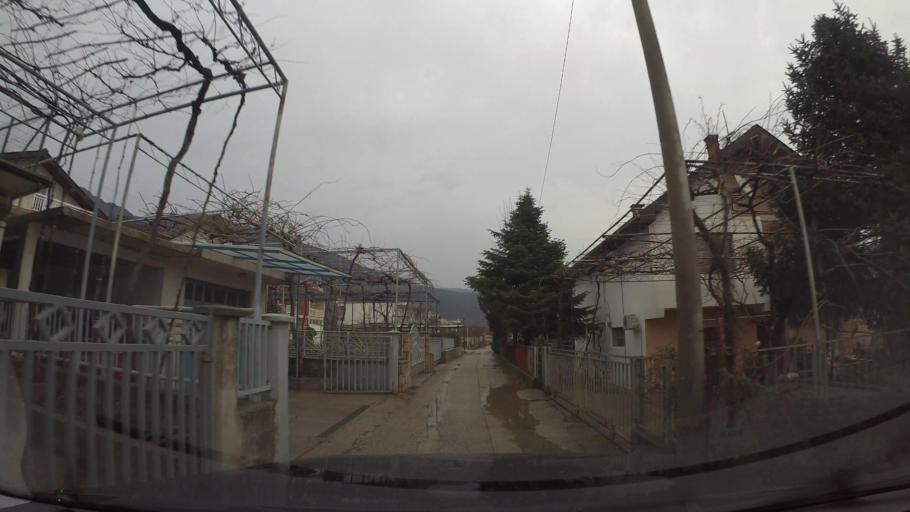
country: BA
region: Federation of Bosnia and Herzegovina
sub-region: Hercegovacko-Bosanski Kanton
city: Mostar
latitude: 43.3611
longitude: 17.8021
